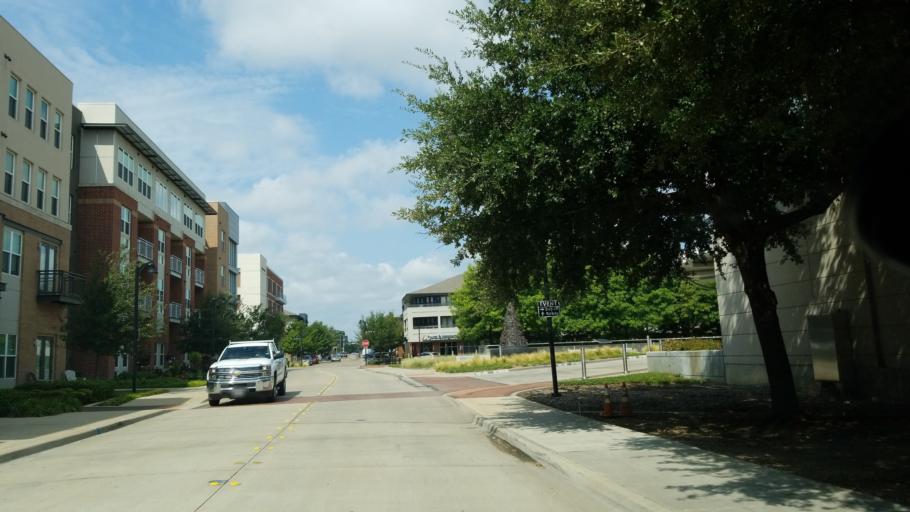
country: US
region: Texas
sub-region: Dallas County
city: Garland
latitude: 32.9144
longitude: -96.6355
